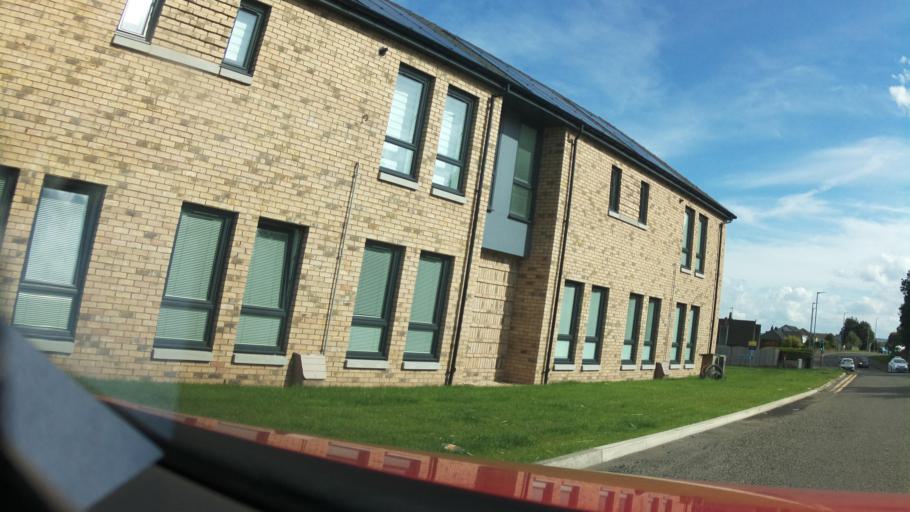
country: GB
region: Scotland
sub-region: Falkirk
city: Larbert
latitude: 56.0293
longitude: -3.8442
